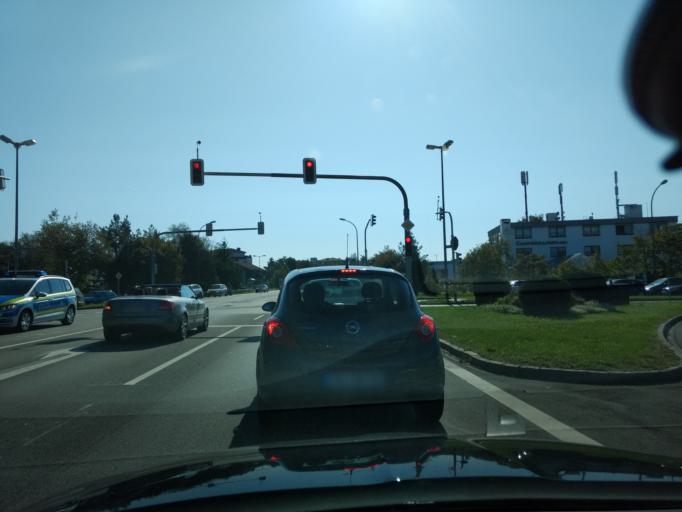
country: DE
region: Bavaria
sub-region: Upper Bavaria
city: Wolfratshausen
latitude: 47.9073
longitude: 11.4300
